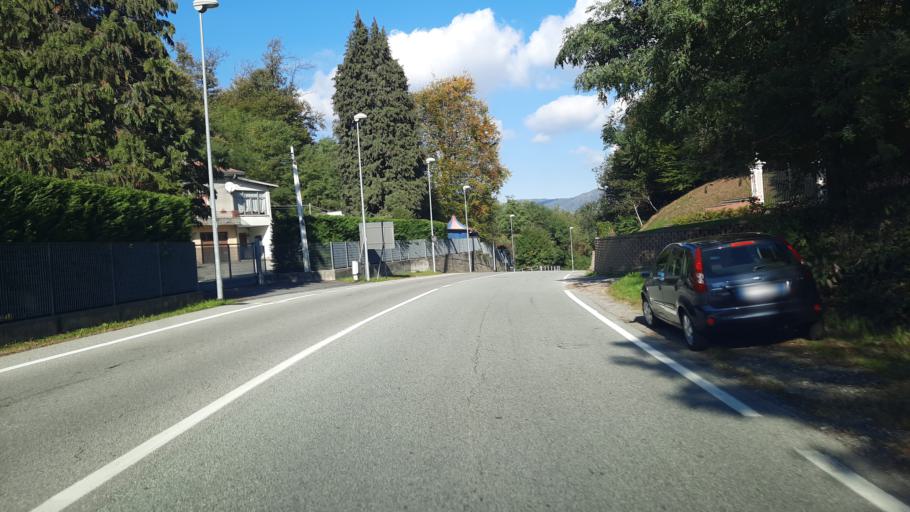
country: IT
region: Piedmont
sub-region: Provincia di Novara
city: Gozzano
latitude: 45.7439
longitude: 8.4243
